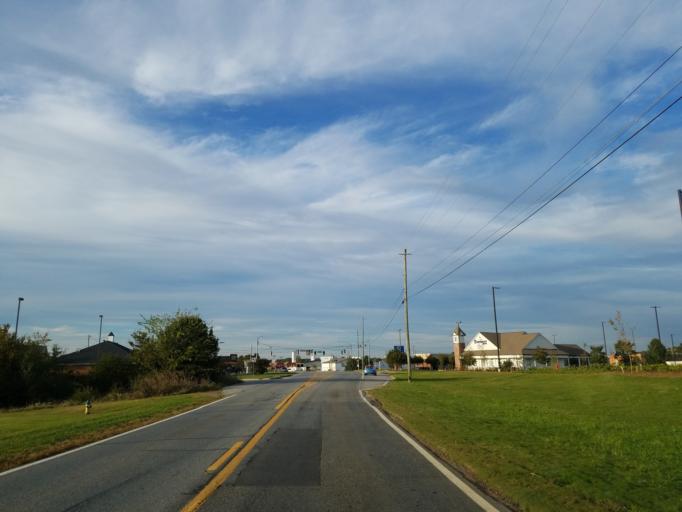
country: US
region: Georgia
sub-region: Bartow County
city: Cartersville
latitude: 34.1484
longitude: -84.8243
